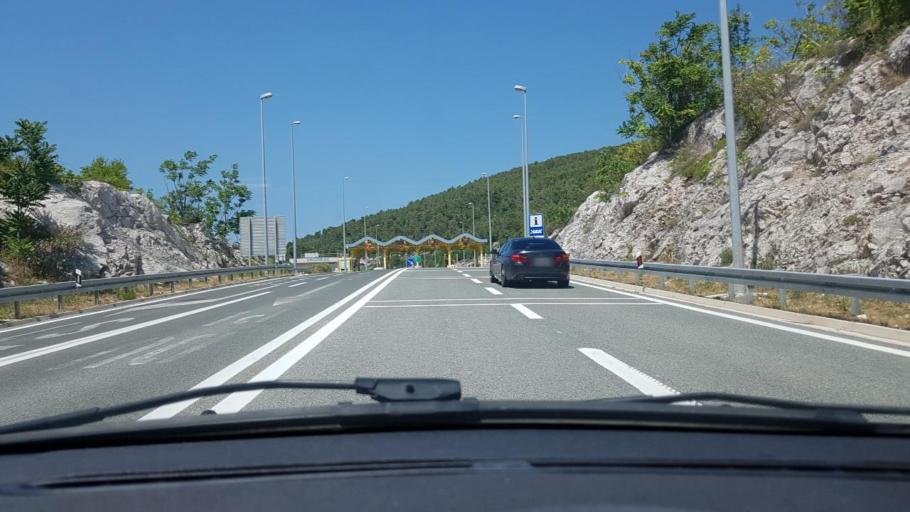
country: HR
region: Splitsko-Dalmatinska
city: Vrgorac
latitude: 43.1904
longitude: 17.3789
